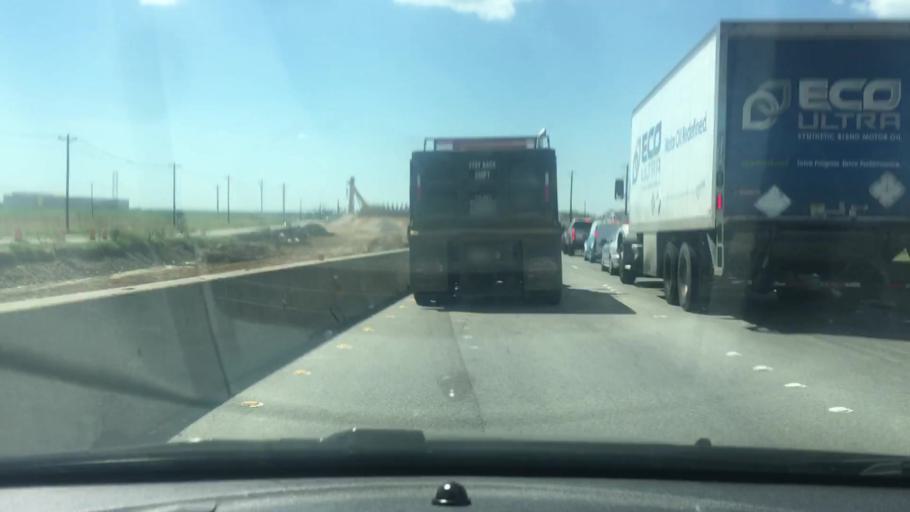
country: US
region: Texas
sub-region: Collin County
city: Prosper
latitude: 33.2190
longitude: -96.8155
